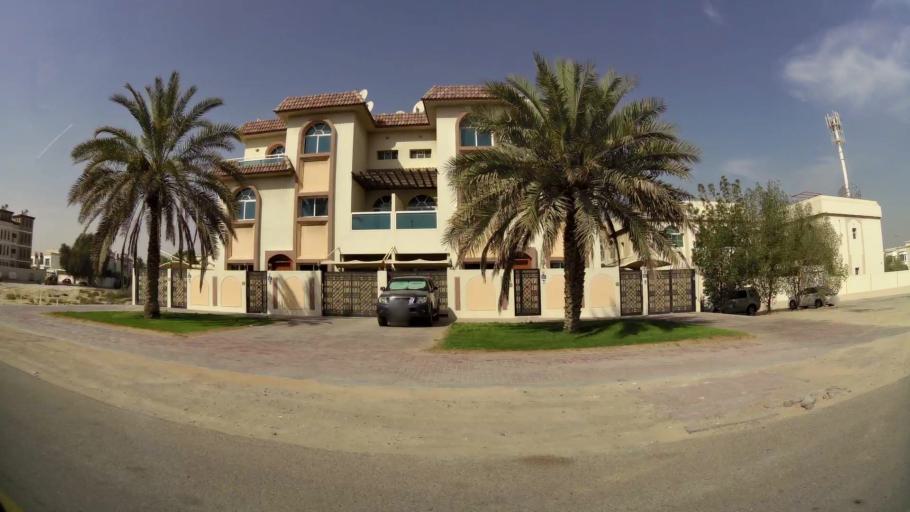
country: AE
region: Ash Shariqah
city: Sharjah
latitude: 25.2186
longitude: 55.4253
